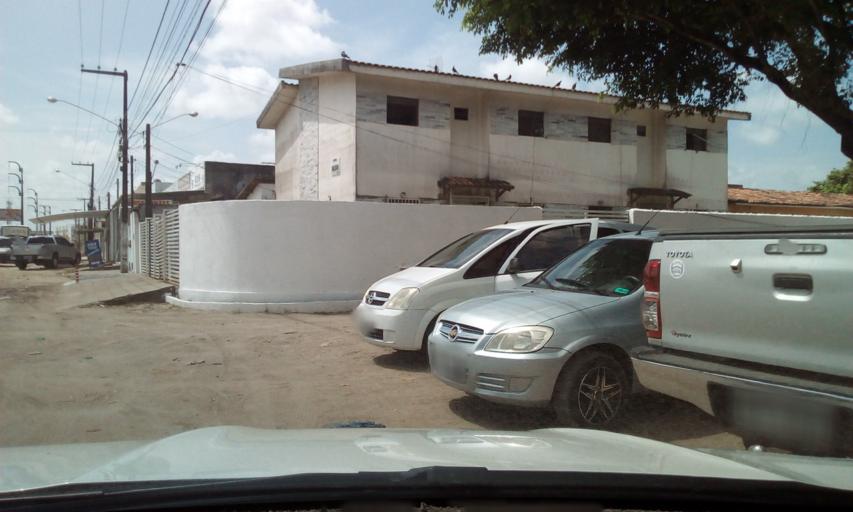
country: BR
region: Paraiba
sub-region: Joao Pessoa
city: Joao Pessoa
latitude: -7.1797
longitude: -34.8703
